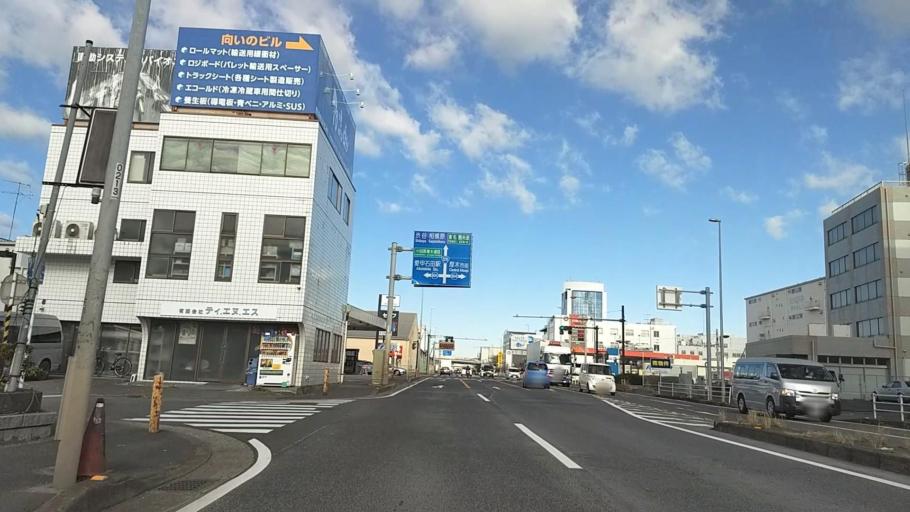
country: JP
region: Kanagawa
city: Atsugi
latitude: 35.4155
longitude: 139.3625
